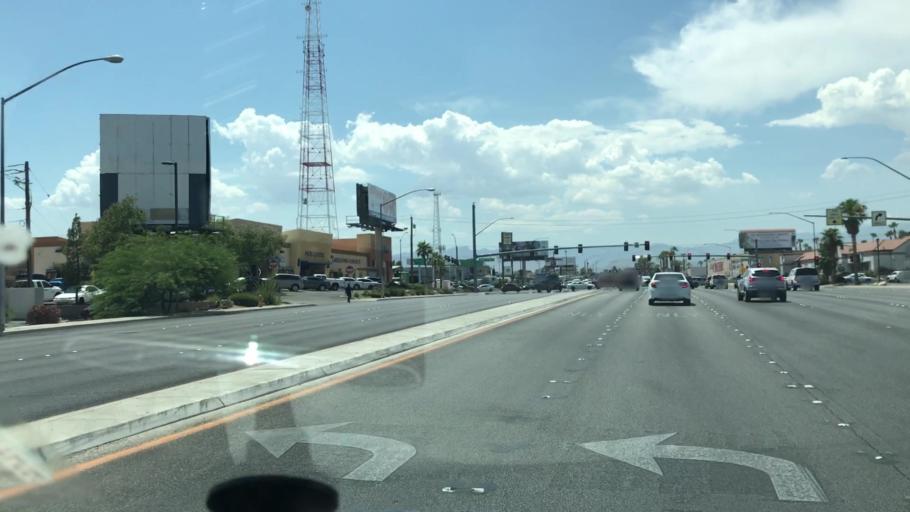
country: US
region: Nevada
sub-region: Clark County
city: Paradise
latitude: 36.1301
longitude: -115.1885
